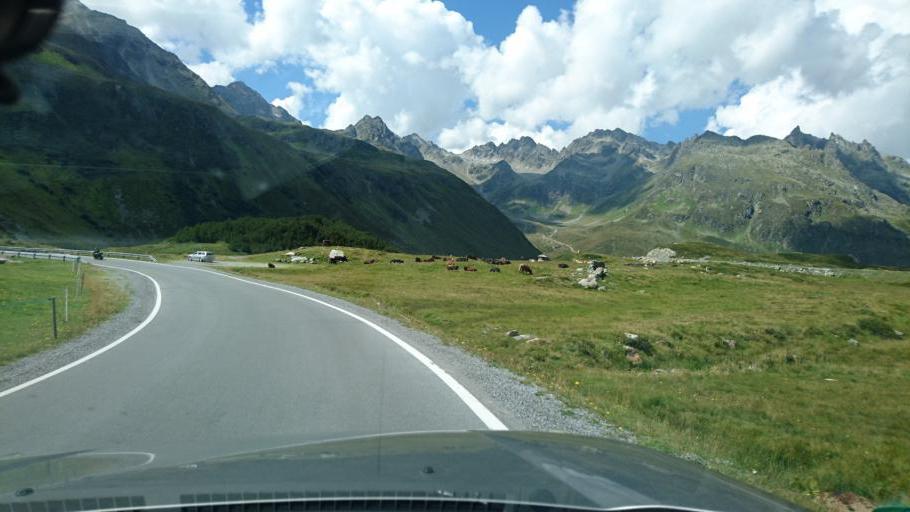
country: AT
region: Vorarlberg
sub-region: Politischer Bezirk Bludenz
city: Gaschurn
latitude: 46.9207
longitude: 10.0692
